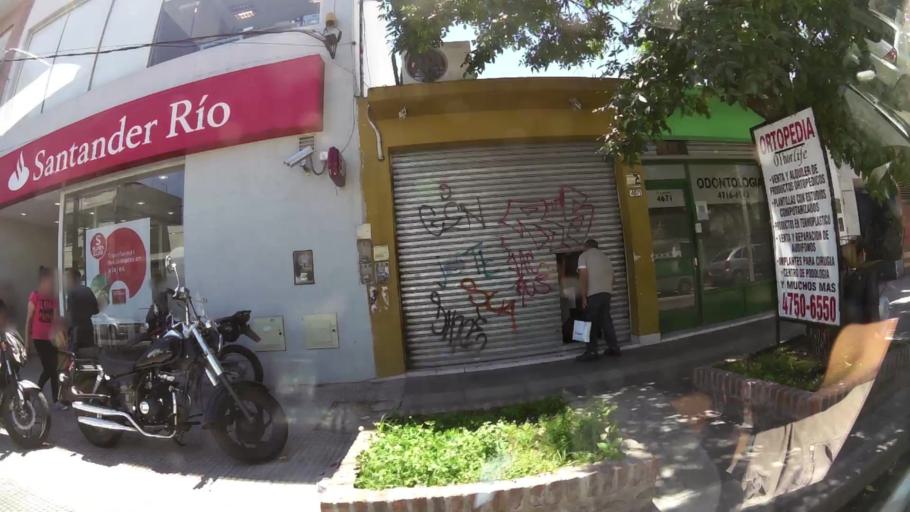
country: AR
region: Buenos Aires
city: Caseros
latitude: -34.6023
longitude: -58.5612
